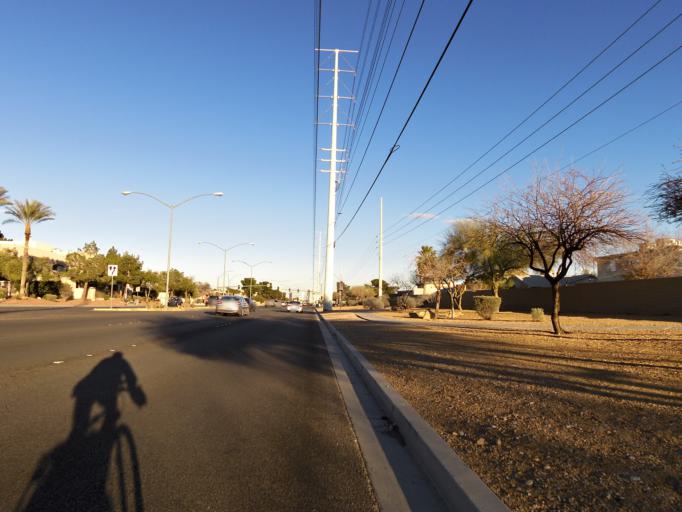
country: US
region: Nevada
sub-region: Clark County
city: Spring Valley
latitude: 36.1145
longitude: -115.2539
